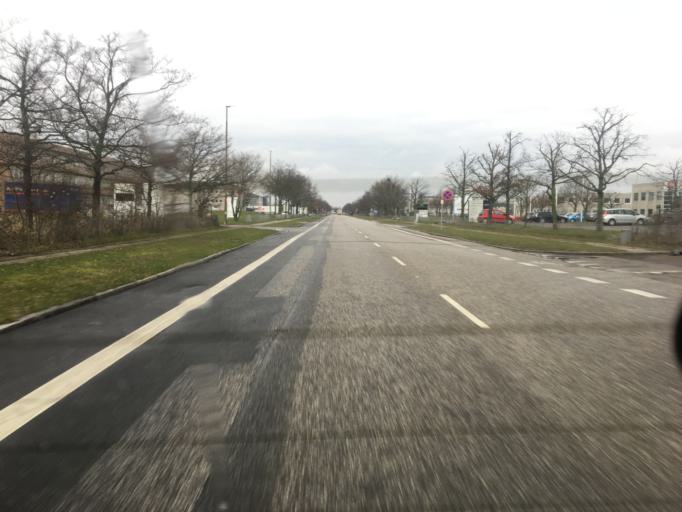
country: DK
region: Capital Region
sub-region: Hvidovre Kommune
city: Hvidovre
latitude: 55.6066
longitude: 12.4892
